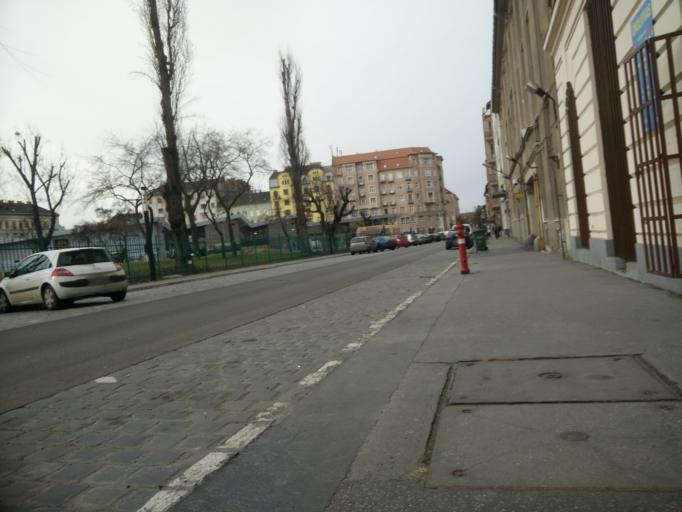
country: HU
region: Budapest
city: Budapest VIII. keruelet
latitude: 47.4944
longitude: 19.0843
